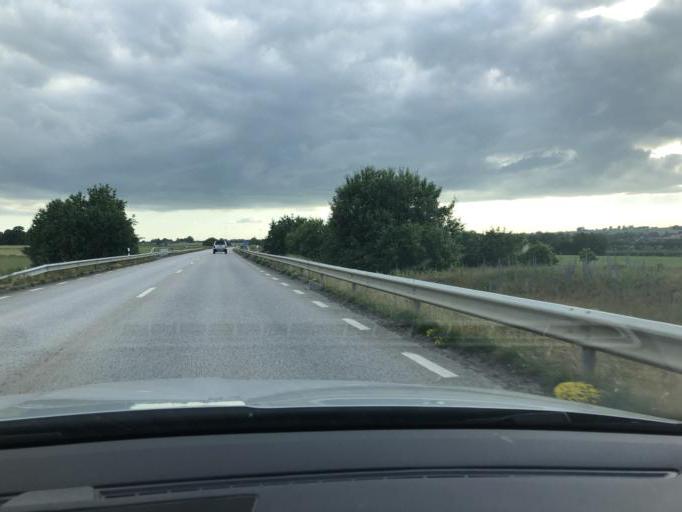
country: SE
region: Skane
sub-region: Simrishamns Kommun
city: Simrishamn
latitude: 55.5409
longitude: 14.3274
